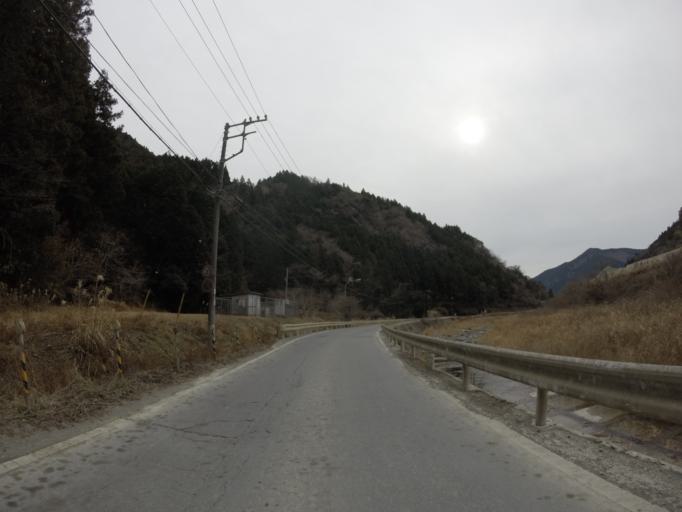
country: JP
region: Shizuoka
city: Fujinomiya
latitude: 35.2388
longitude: 138.5348
